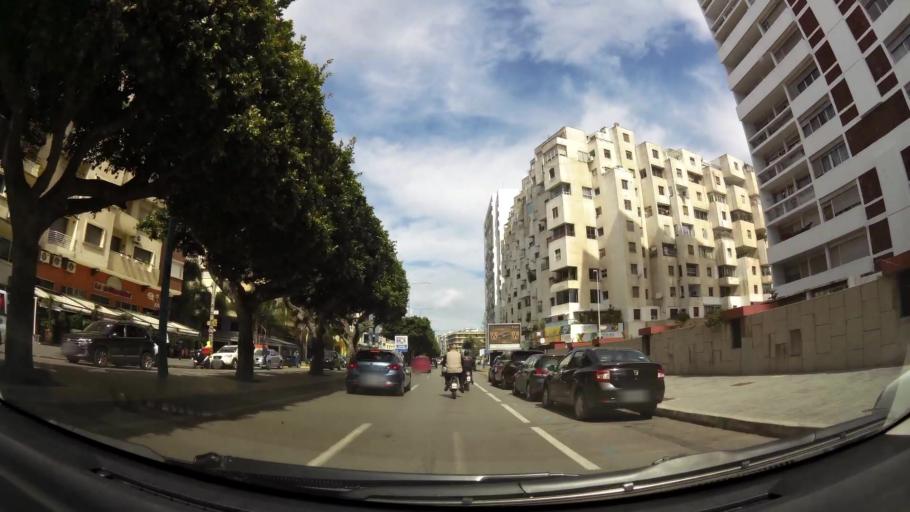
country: MA
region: Grand Casablanca
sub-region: Casablanca
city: Casablanca
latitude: 33.5835
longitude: -7.6415
